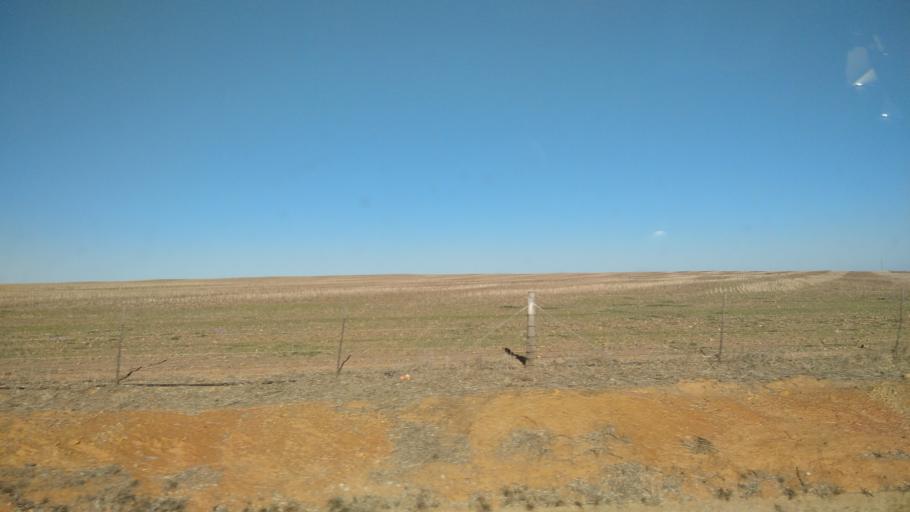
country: ZA
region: Western Cape
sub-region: West Coast District Municipality
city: Malmesbury
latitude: -33.3520
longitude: 18.6421
